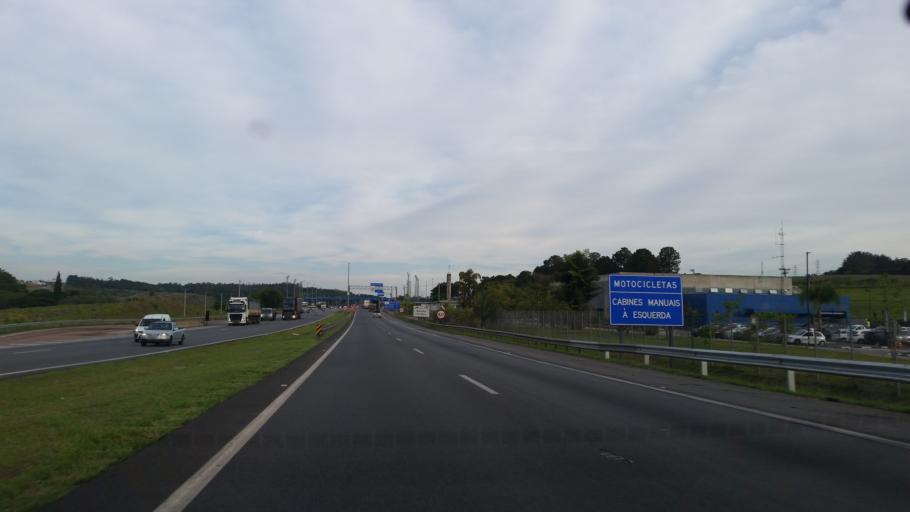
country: BR
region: Sao Paulo
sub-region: Itatiba
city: Itatiba
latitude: -22.9514
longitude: -46.8647
